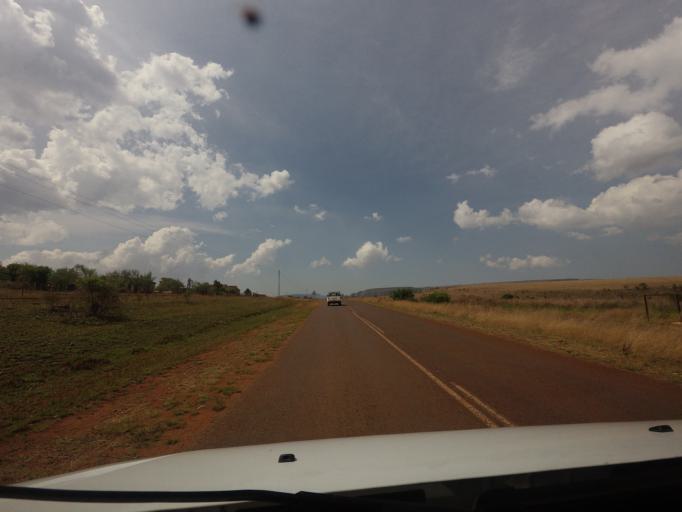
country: ZA
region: Mpumalanga
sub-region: Ehlanzeni District
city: Graksop
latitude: -24.6611
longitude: 30.8161
